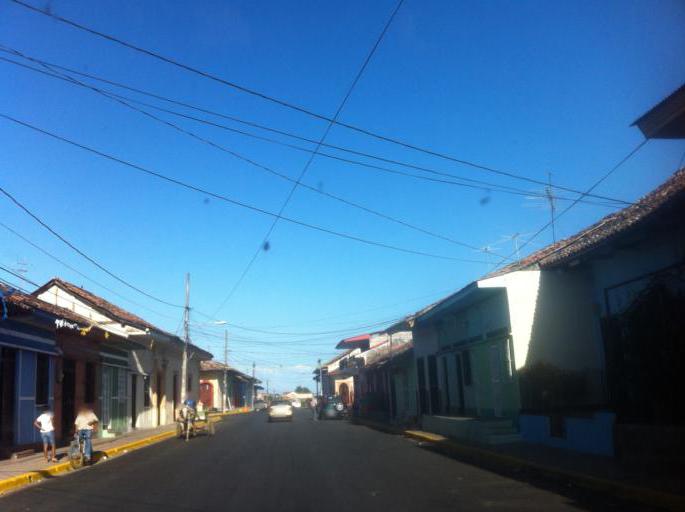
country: NI
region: Granada
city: Granada
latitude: 11.9275
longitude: -85.9612
